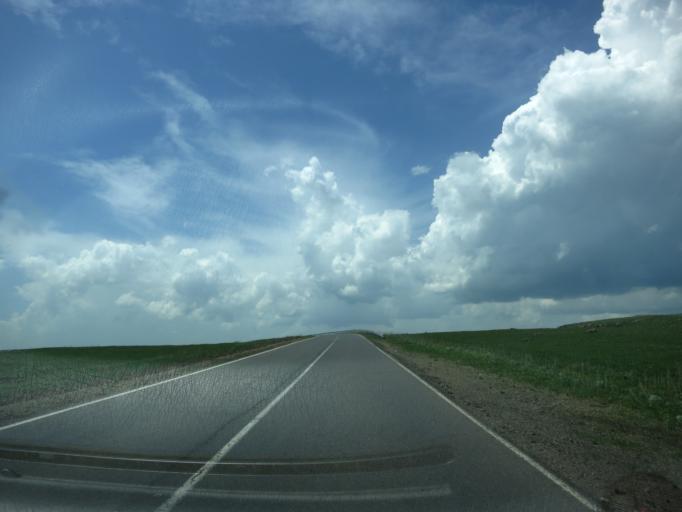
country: GE
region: Samtskhe-Javakheti
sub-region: Ninotsminda
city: Ninotsminda
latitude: 41.2916
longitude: 43.7254
